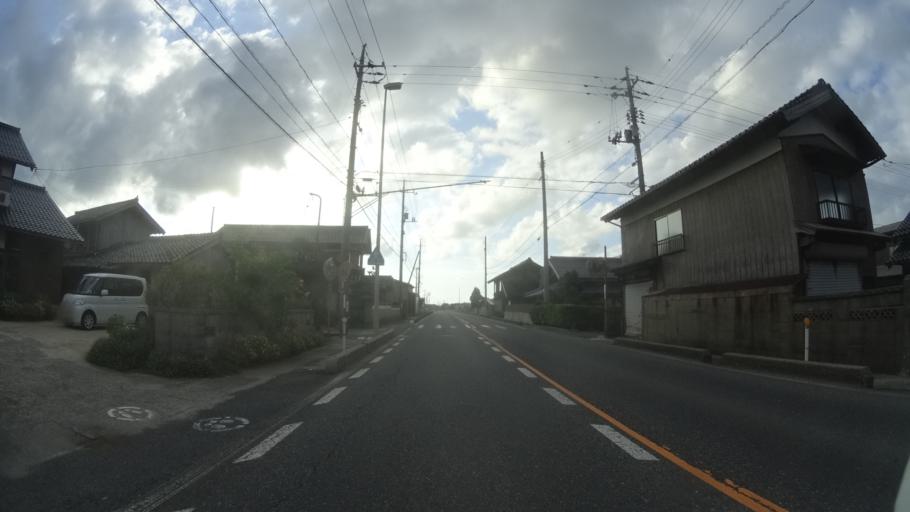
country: JP
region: Tottori
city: Kurayoshi
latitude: 35.5222
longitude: 133.5972
